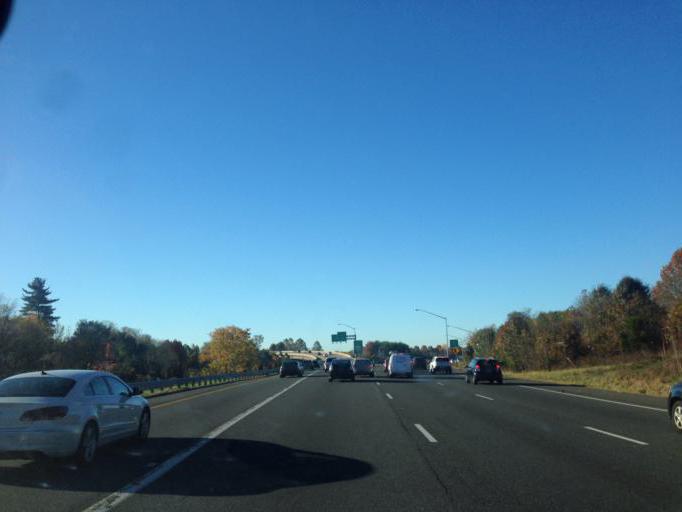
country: US
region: Maryland
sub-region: Howard County
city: Columbia
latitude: 39.2561
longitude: -76.8213
